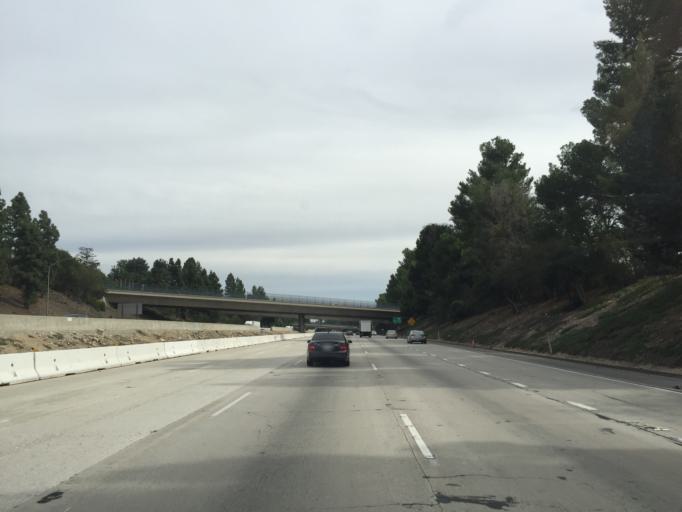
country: US
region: California
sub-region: Los Angeles County
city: La Crescenta-Montrose
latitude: 34.2169
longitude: -118.2374
